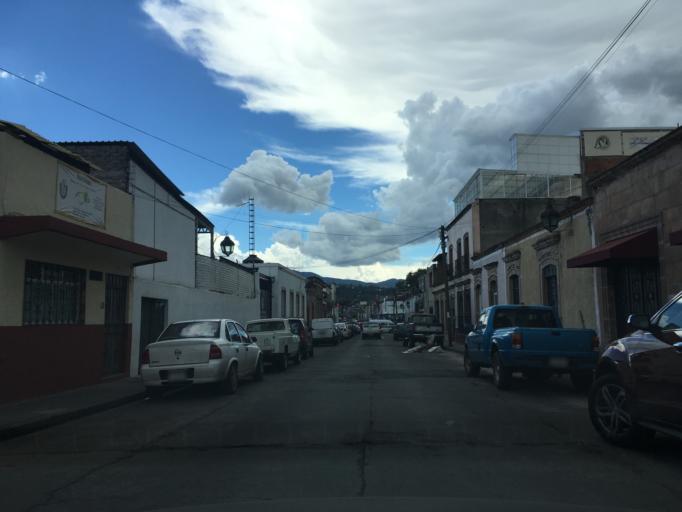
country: MX
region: Michoacan
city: Morelia
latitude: 19.6968
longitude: -101.1916
